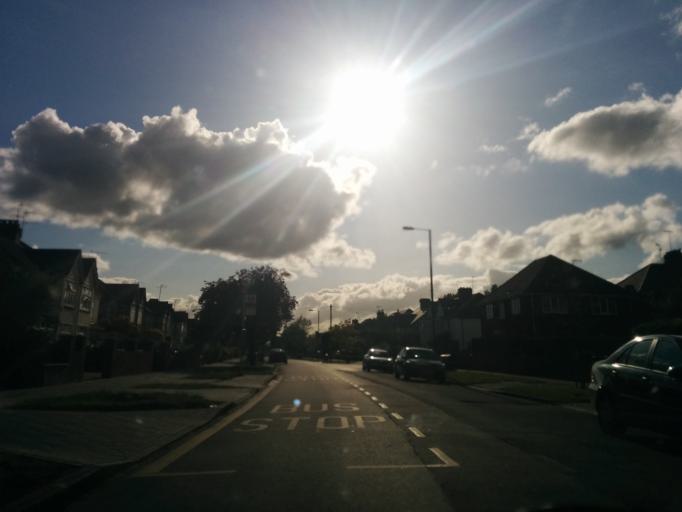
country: GB
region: England
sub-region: Greater London
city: Greenhill
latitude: 51.5753
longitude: -0.3507
